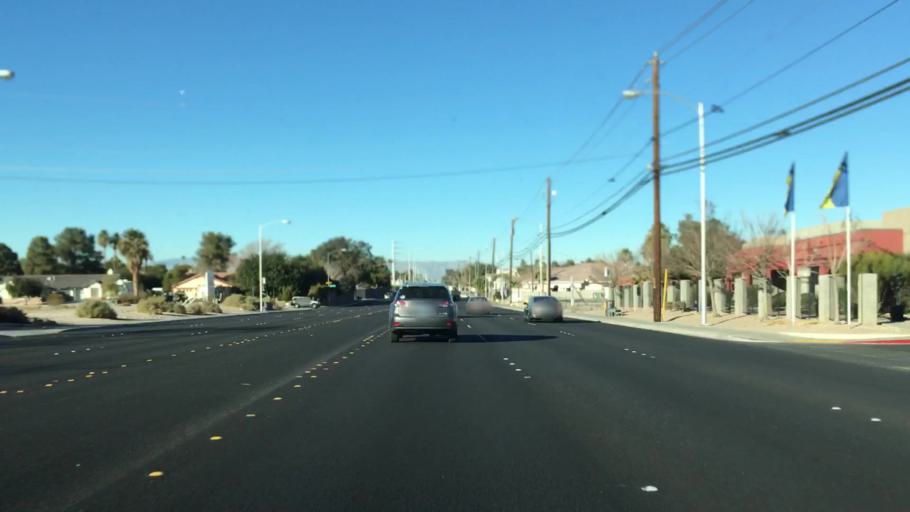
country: US
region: Nevada
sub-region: Clark County
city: Whitney
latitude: 36.0815
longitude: -115.1009
